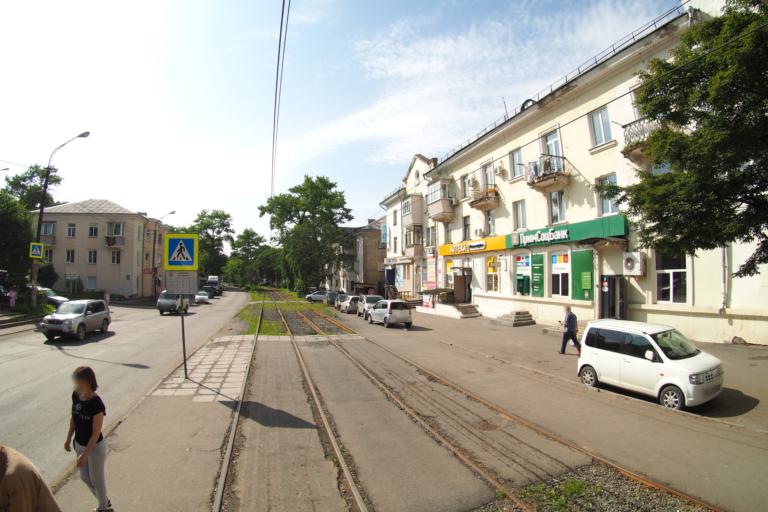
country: RU
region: Primorskiy
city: Vladivostok
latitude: 43.1005
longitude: 131.9492
